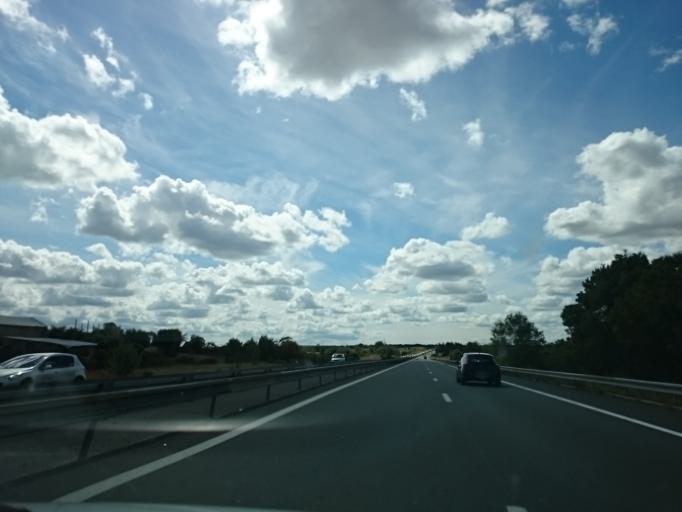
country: FR
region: Pays de la Loire
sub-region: Departement de la Loire-Atlantique
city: Ancenis
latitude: 47.4105
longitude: -1.1555
